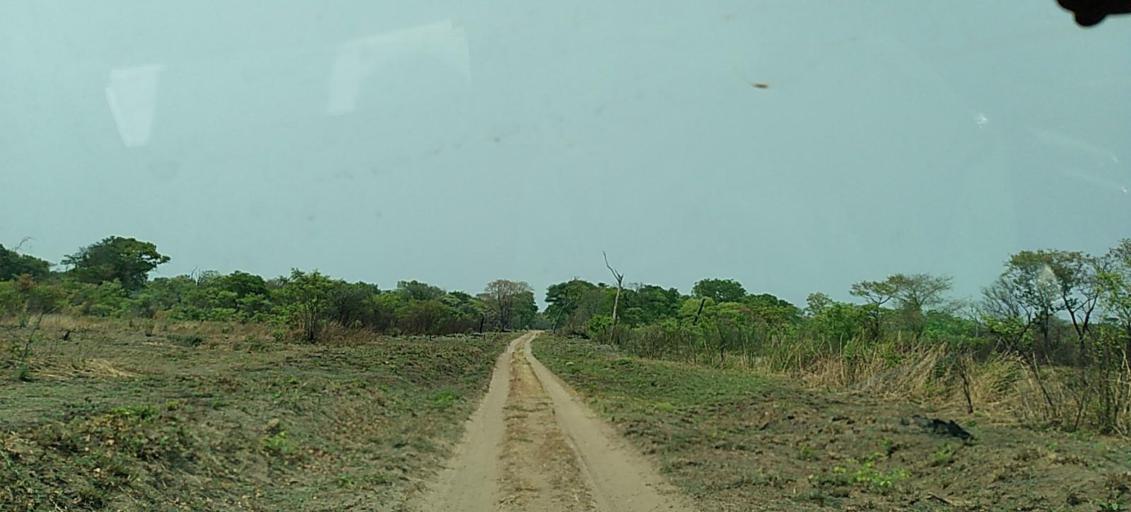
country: ZM
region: North-Western
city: Zambezi
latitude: -13.9463
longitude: 23.2234
